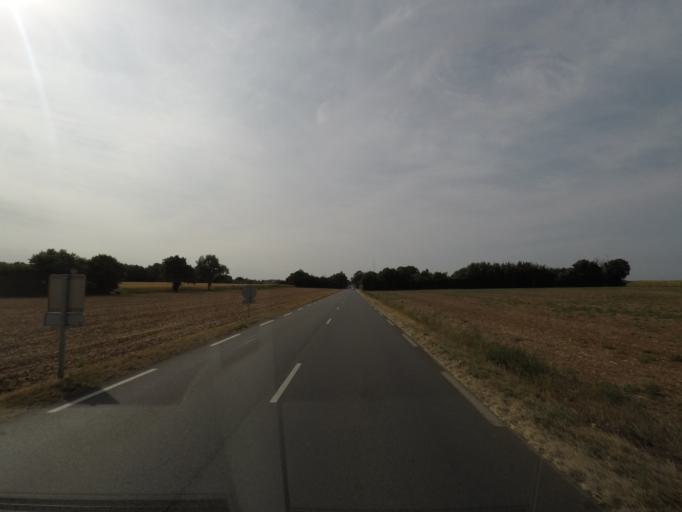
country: FR
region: Poitou-Charentes
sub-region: Departement des Deux-Sevres
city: Lezay
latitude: 46.1742
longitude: -0.0062
